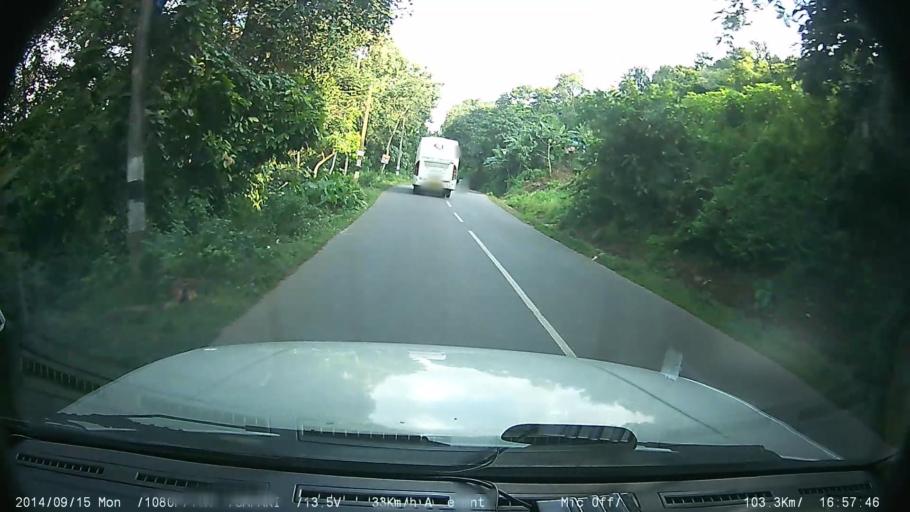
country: IN
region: Kerala
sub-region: Kottayam
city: Palackattumala
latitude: 9.8253
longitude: 76.5840
